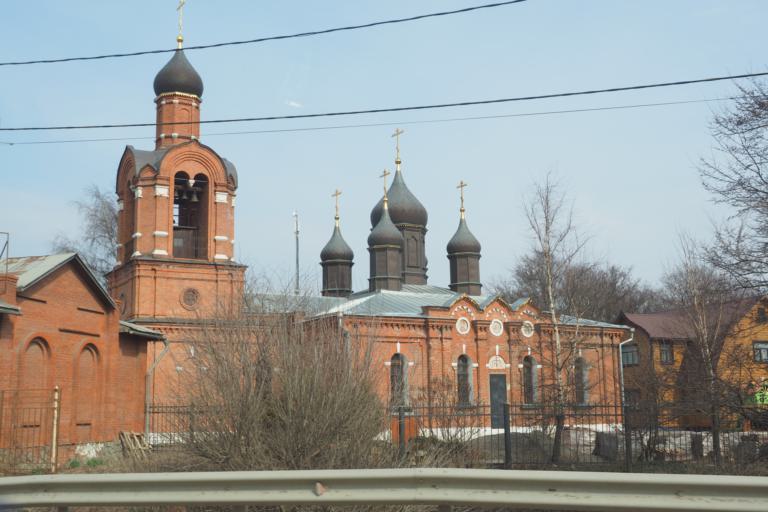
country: RU
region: Moskovskaya
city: Bronnitsy
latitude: 55.3953
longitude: 38.3221
